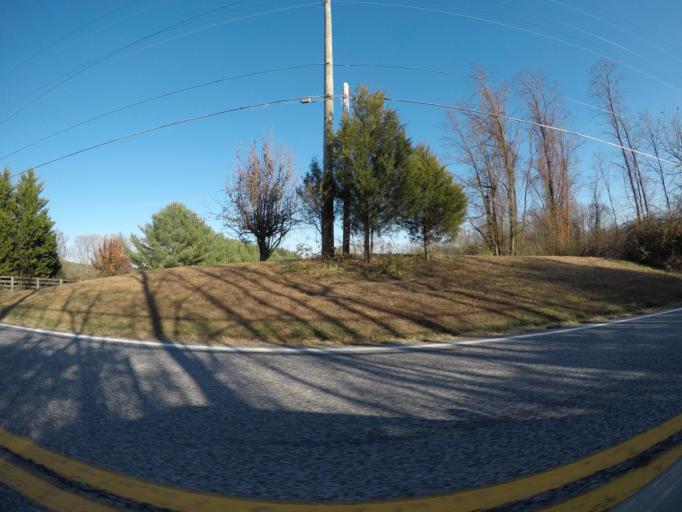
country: US
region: Maryland
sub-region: Harford County
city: South Bel Air
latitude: 39.5794
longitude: -76.2586
